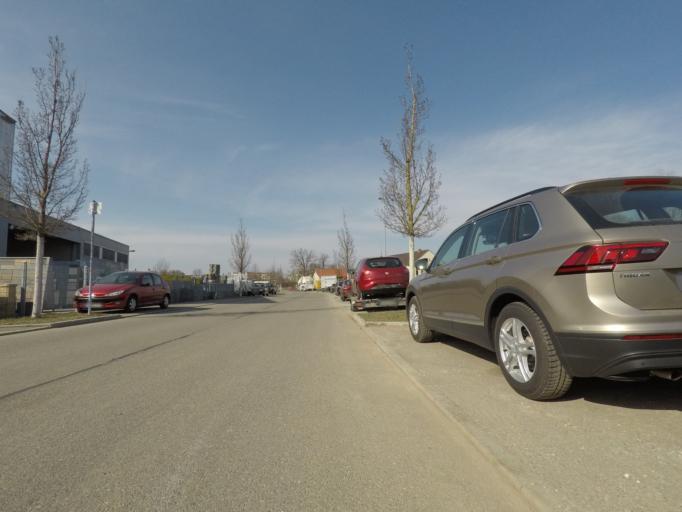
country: DE
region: Baden-Wuerttemberg
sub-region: Tuebingen Region
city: Metzingen
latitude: 48.5316
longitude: 9.2915
